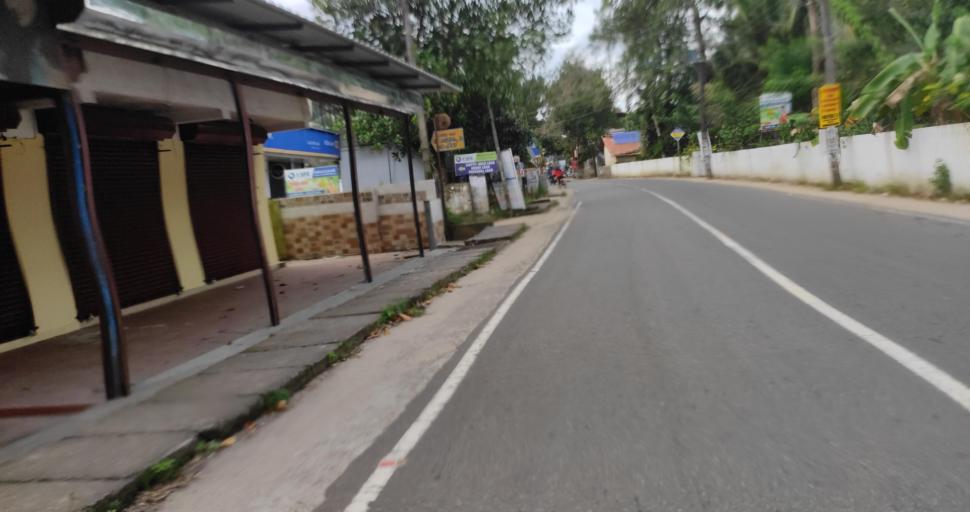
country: IN
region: Kerala
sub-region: Alappuzha
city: Shertallai
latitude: 9.6559
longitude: 76.3180
